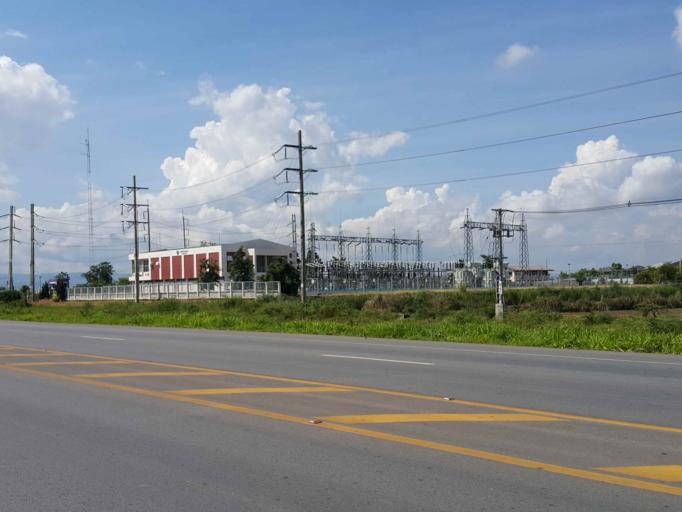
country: TH
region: Chiang Mai
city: San Kamphaeng
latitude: 18.7369
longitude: 99.0866
